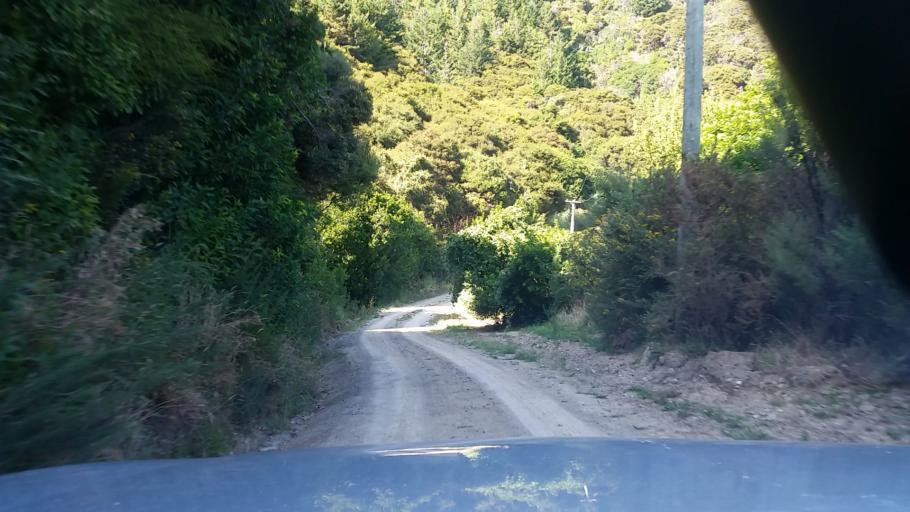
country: NZ
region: Marlborough
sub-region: Marlborough District
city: Picton
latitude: -41.3147
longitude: 174.1748
